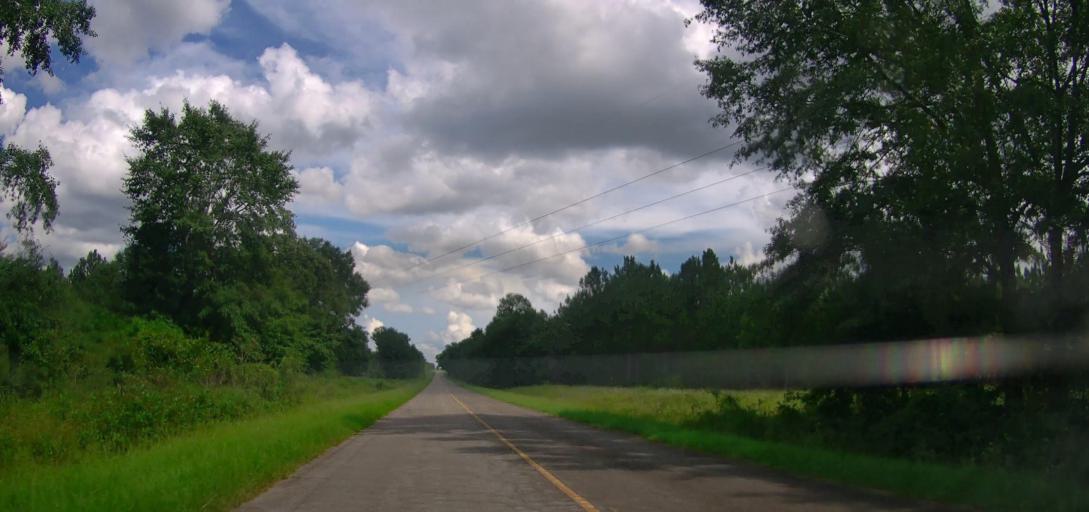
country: US
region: Georgia
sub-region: Taylor County
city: Butler
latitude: 32.5922
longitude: -84.3672
